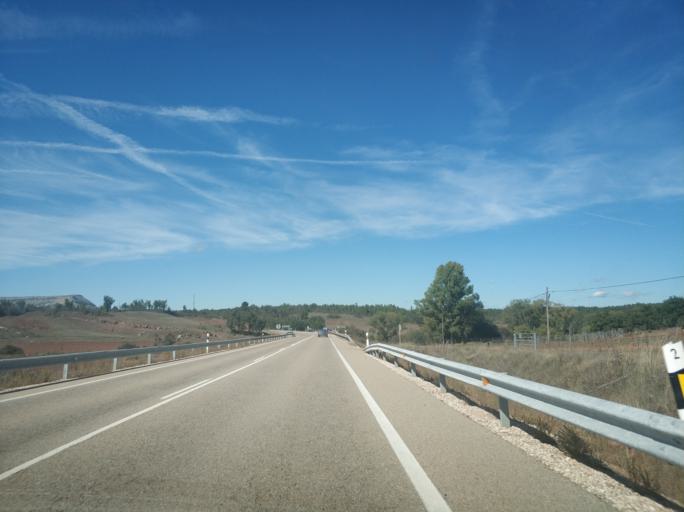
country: ES
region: Castille and Leon
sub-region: Provincia de Burgos
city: Pinilla de los Barruecos
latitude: 41.9354
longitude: -3.2846
